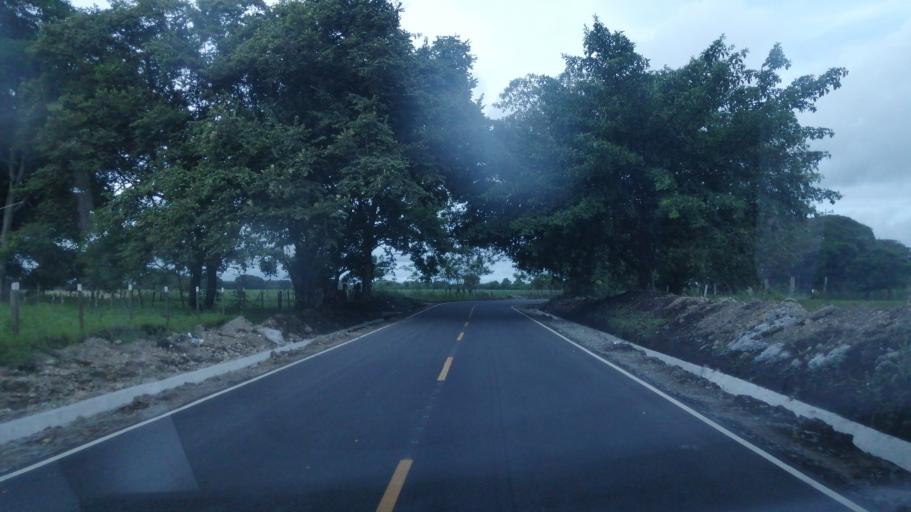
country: PA
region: Chiriqui
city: Alanje
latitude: 8.4315
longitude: -82.5180
